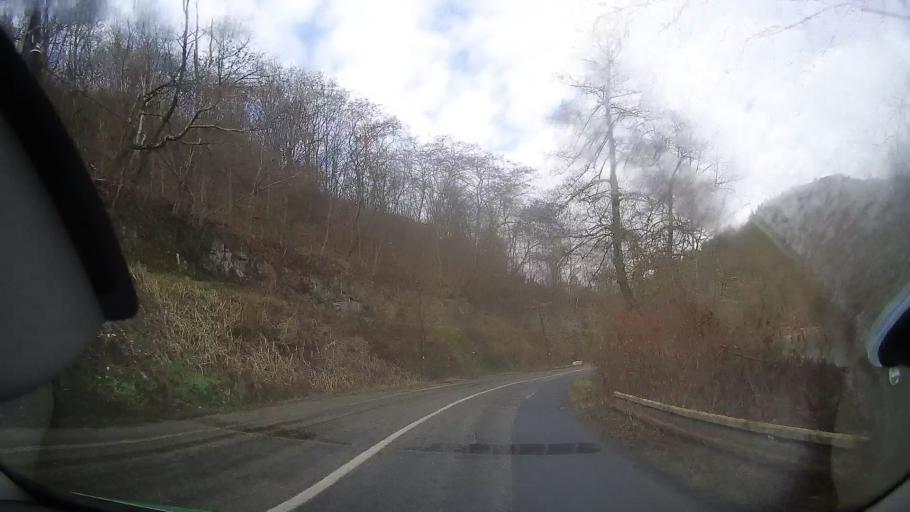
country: RO
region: Alba
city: Salciua de Sus
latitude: 46.4238
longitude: 23.4543
